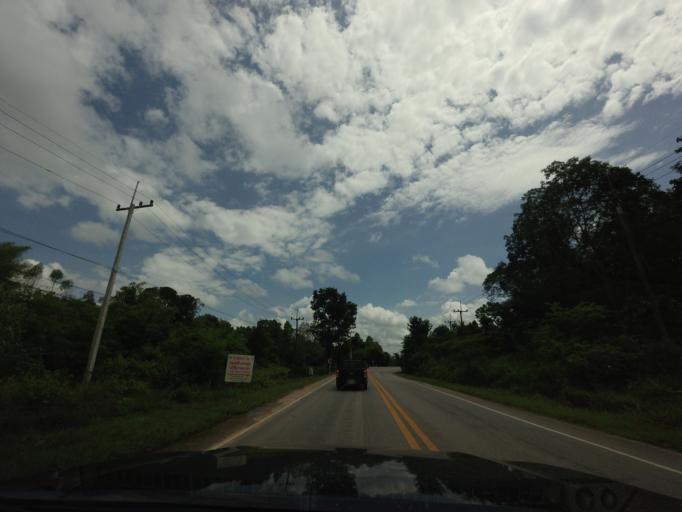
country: TH
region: Nong Khai
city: Pho Tak
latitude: 17.8074
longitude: 102.3294
